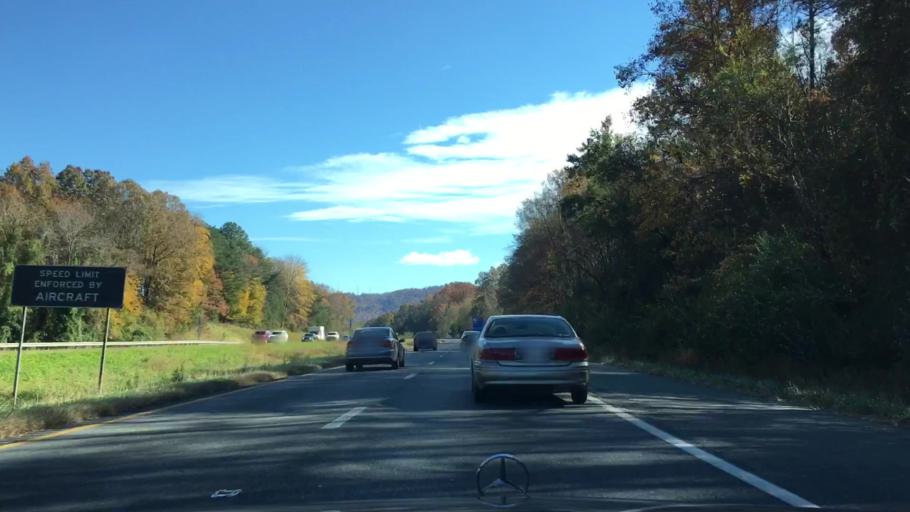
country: US
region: Virginia
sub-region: City of Charlottesville
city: Charlottesville
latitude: 38.0161
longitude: -78.5306
